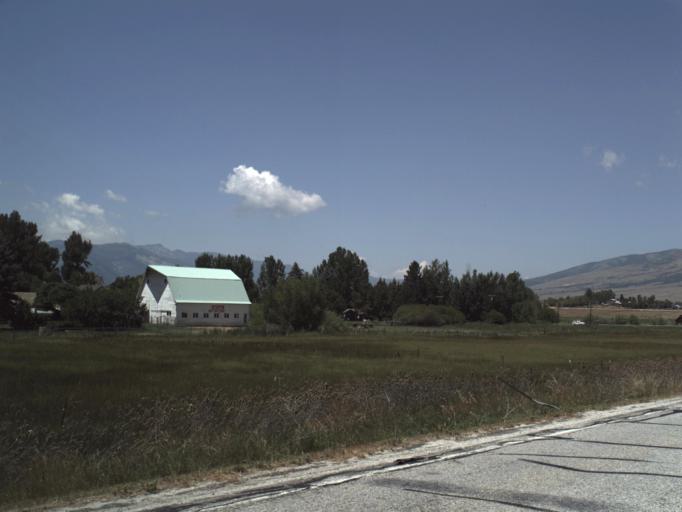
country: US
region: Utah
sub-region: Weber County
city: Wolf Creek
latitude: 41.2571
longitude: -111.7613
